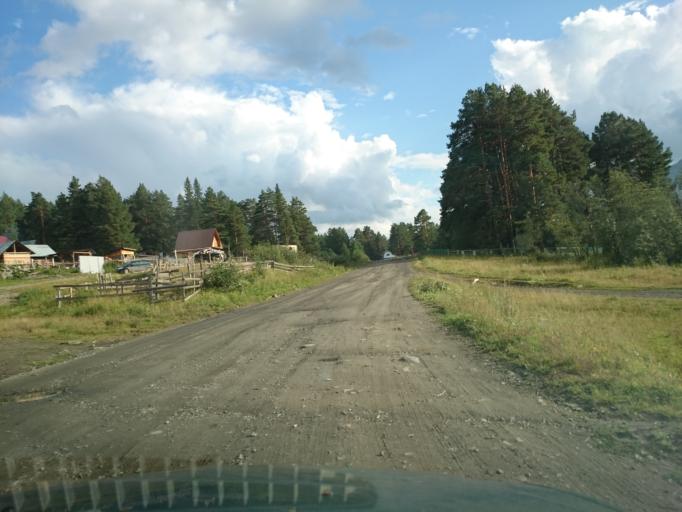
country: RU
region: Bashkortostan
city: Beloretsk
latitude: 54.0455
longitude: 58.3309
